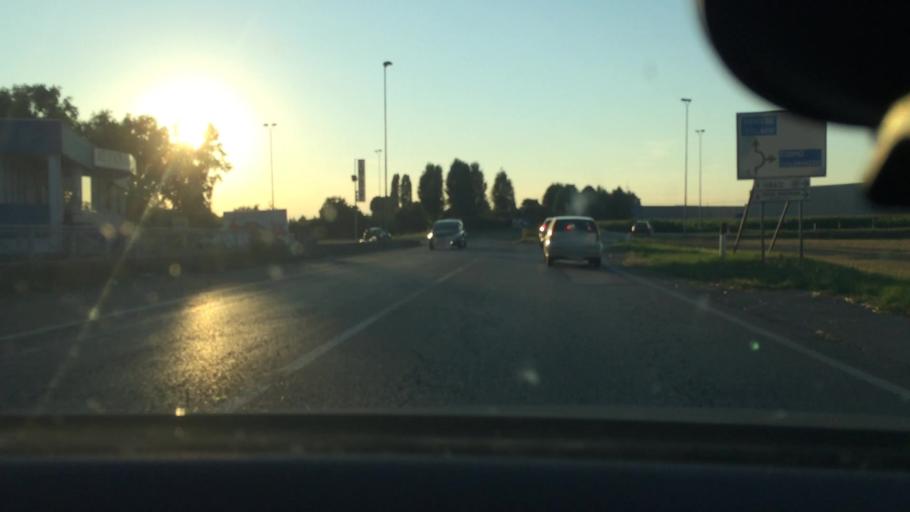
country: IT
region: Lombardy
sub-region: Provincia di Varese
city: Gerenzano
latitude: 45.6481
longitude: 8.9932
